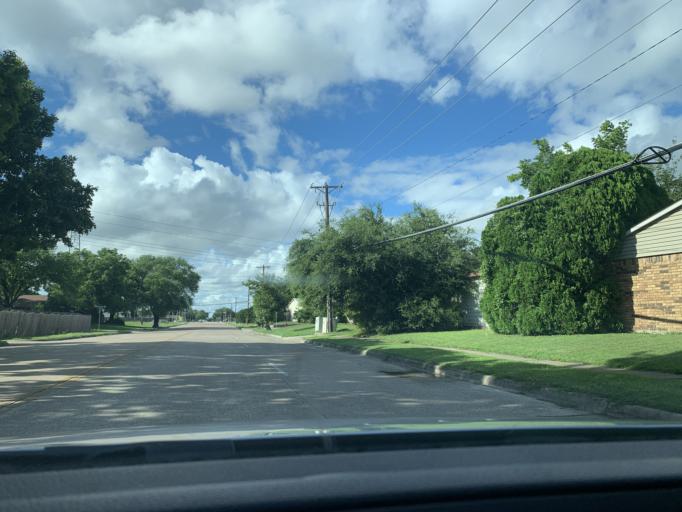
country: US
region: Texas
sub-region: Dallas County
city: Grand Prairie
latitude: 32.6554
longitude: -97.0278
